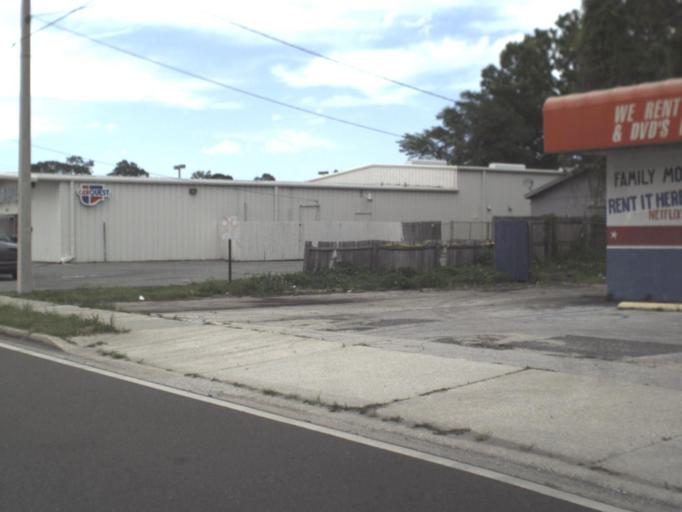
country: US
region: Florida
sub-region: Clay County
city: Bellair-Meadowbrook Terrace
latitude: 30.2463
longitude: -81.7430
